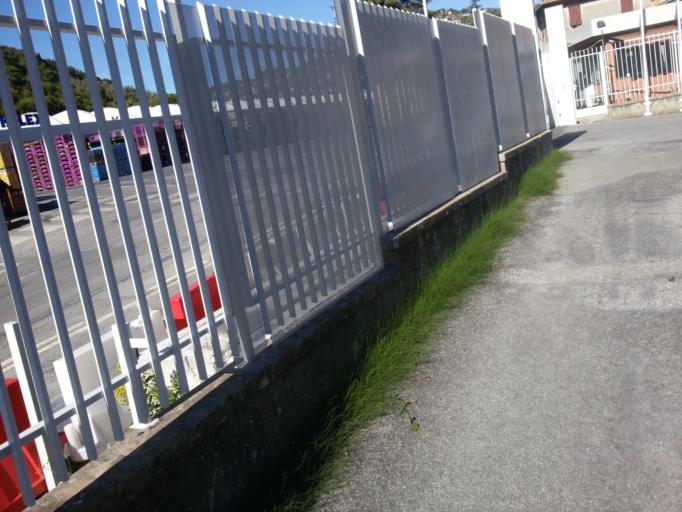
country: IT
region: Liguria
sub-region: Provincia di Genova
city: Chiavari
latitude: 44.3306
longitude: 9.3223
